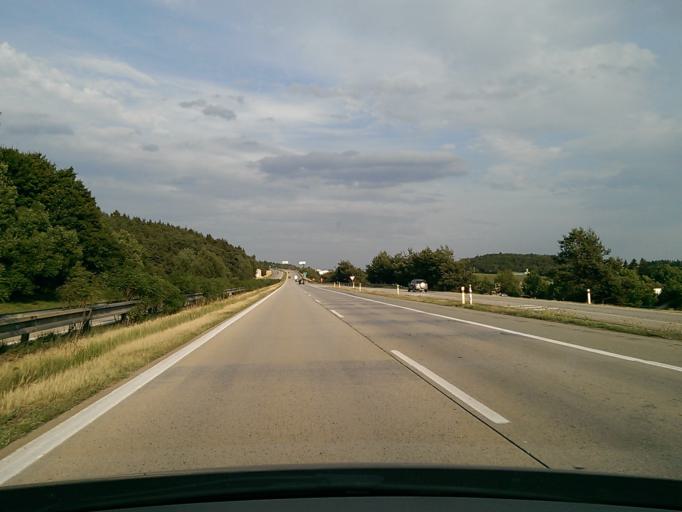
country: CZ
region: Vysocina
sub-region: Okres Zd'ar nad Sazavou
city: Velke Mezirici
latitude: 49.3693
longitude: 15.9743
